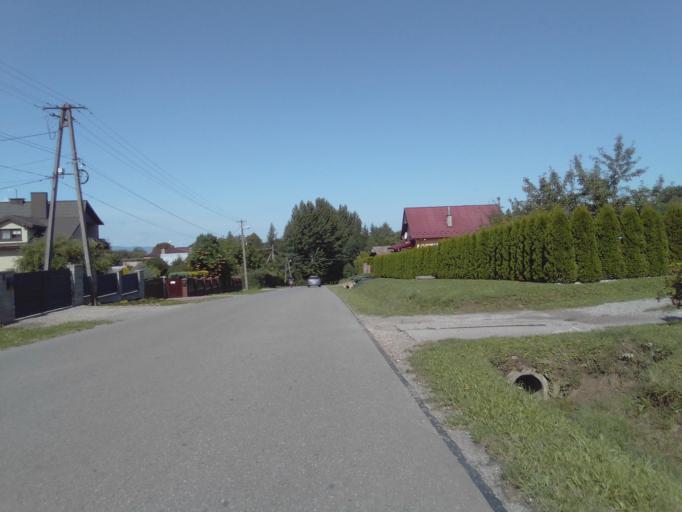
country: PL
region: Subcarpathian Voivodeship
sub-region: Powiat krosnienski
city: Chorkowka
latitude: 49.6024
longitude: 21.6837
